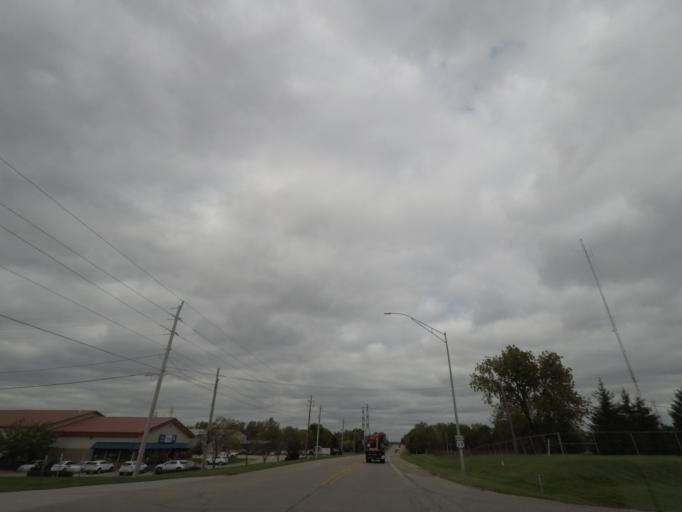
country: US
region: Iowa
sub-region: Polk County
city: Saylorville
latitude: 41.6695
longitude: -93.6008
